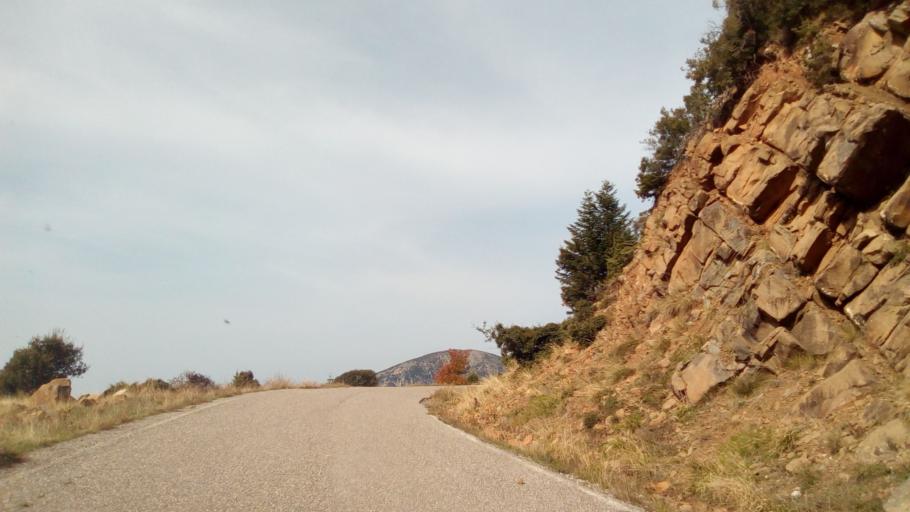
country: GR
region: West Greece
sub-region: Nomos Aitolias kai Akarnanias
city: Thermo
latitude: 38.5612
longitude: 21.8228
